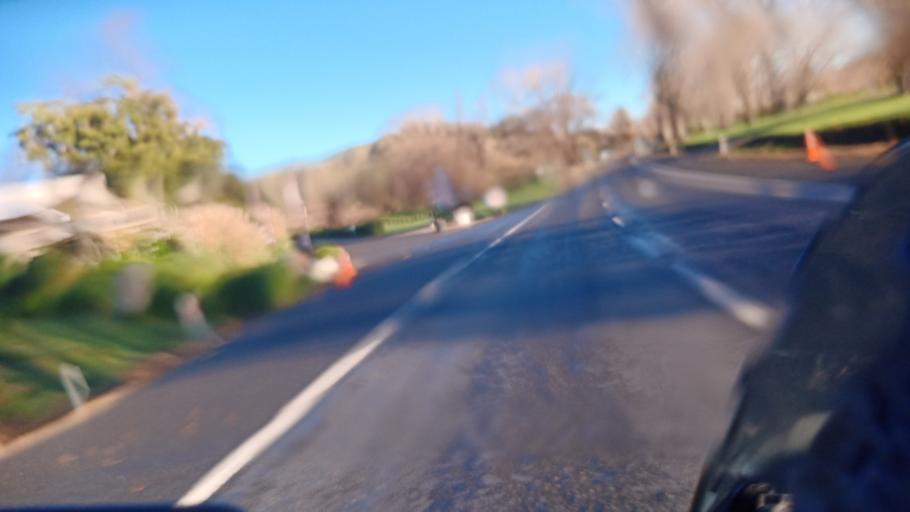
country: NZ
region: Hawke's Bay
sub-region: Wairoa District
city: Wairoa
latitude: -39.0406
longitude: 177.3860
